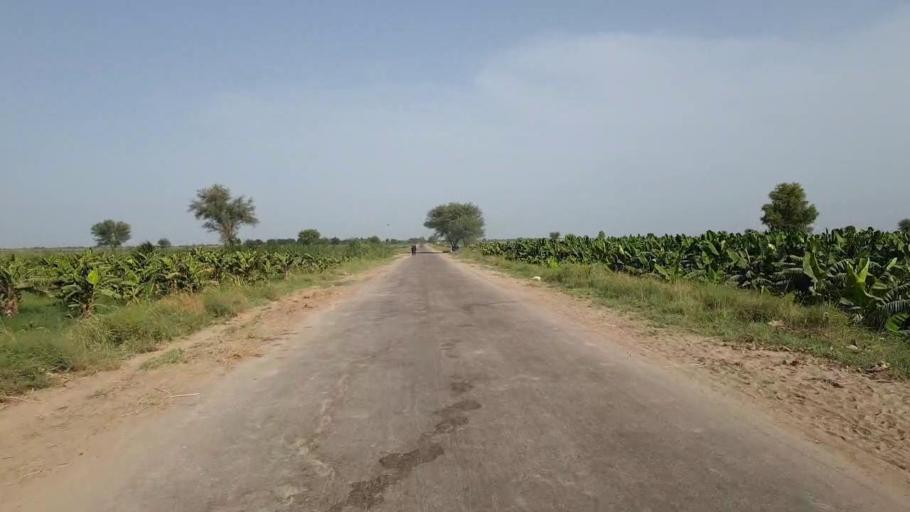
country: PK
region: Sindh
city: Sakrand
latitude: 26.2838
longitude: 68.2639
